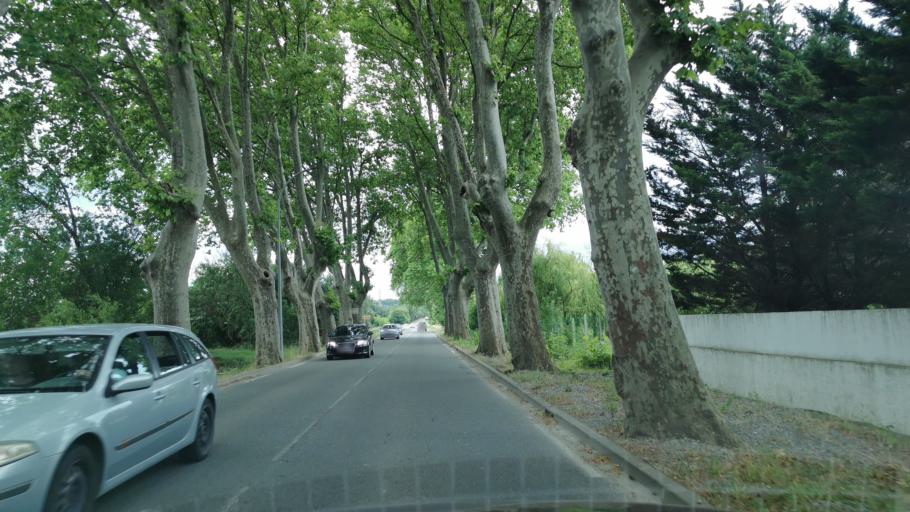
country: FR
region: Languedoc-Roussillon
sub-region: Departement de l'Aude
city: Saint-Marcel-sur-Aude
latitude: 43.2406
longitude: 2.9249
